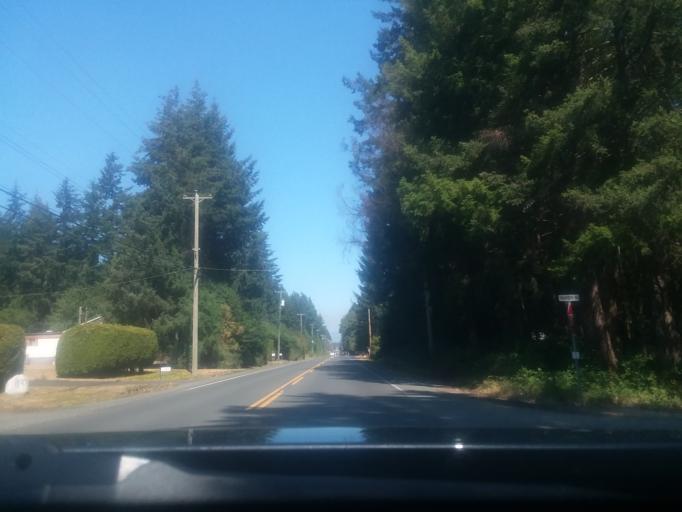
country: CA
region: British Columbia
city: Courtenay
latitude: 49.7065
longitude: -124.9340
